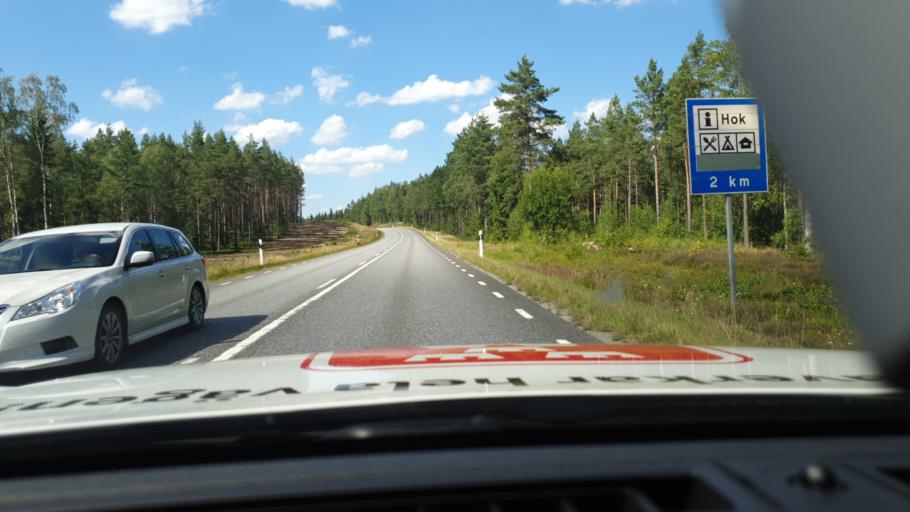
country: SE
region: Joenkoeping
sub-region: Vaggeryds Kommun
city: Vaggeryd
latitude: 57.4968
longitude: 14.2927
